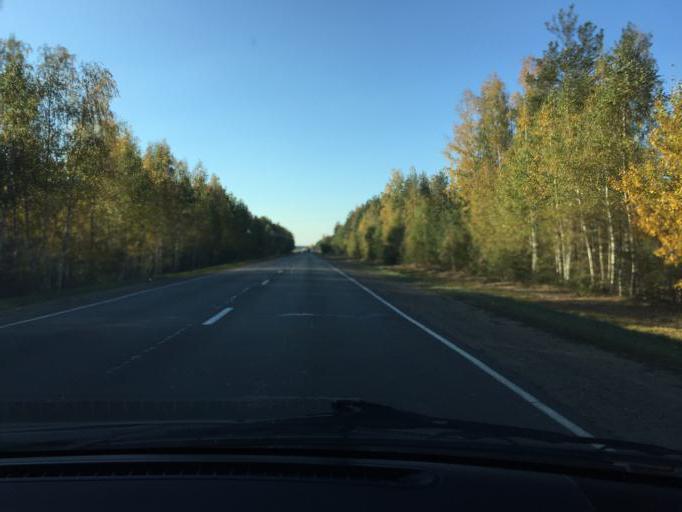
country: BY
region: Brest
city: Luninyets
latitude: 52.2703
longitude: 26.9962
